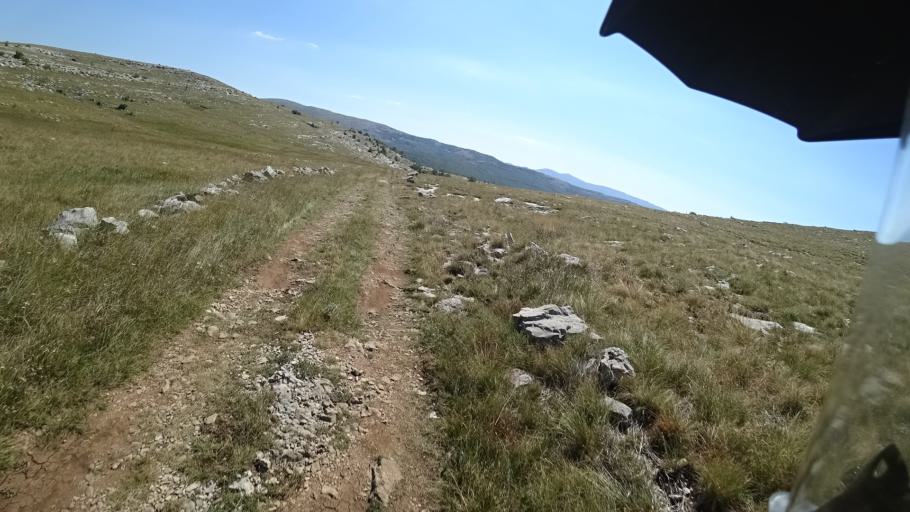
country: HR
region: Splitsko-Dalmatinska
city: Hrvace
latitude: 43.8984
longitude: 16.5897
